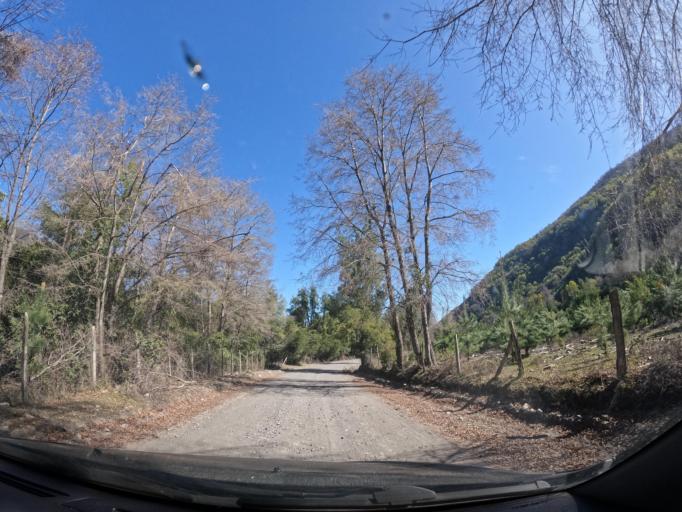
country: CL
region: Maule
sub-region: Provincia de Linares
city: Longavi
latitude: -36.2279
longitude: -71.3926
